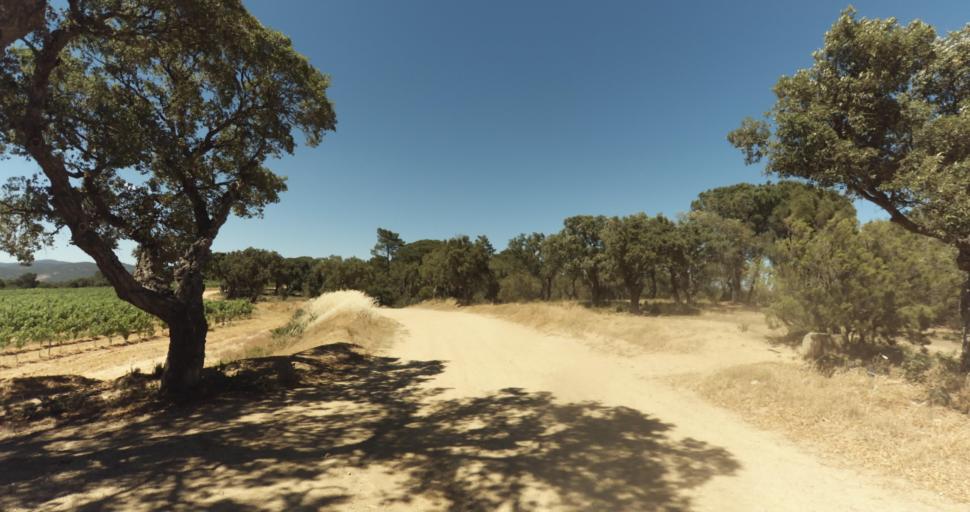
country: FR
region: Provence-Alpes-Cote d'Azur
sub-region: Departement du Var
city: Gassin
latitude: 43.2435
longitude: 6.5610
